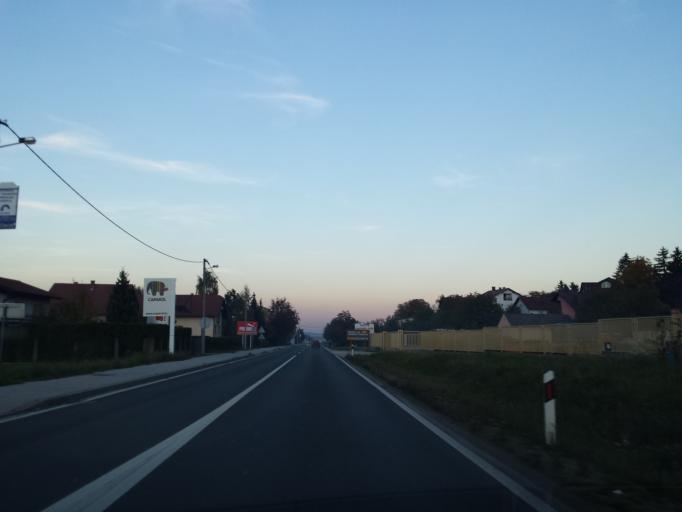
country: HR
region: Zagrebacka
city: Kerestinec
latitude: 45.7977
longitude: 15.7687
